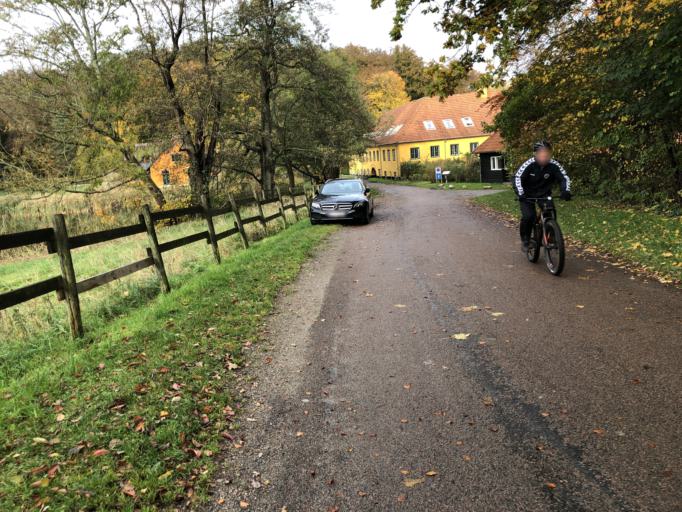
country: DK
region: Capital Region
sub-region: Lyngby-Tarbaek Kommune
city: Kongens Lyngby
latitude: 55.8012
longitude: 12.5140
